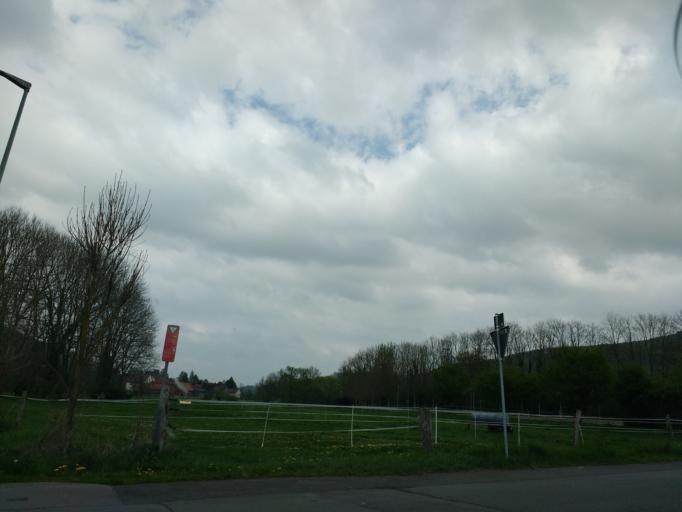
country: DE
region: Lower Saxony
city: Bad Pyrmont
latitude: 51.9815
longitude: 9.2823
